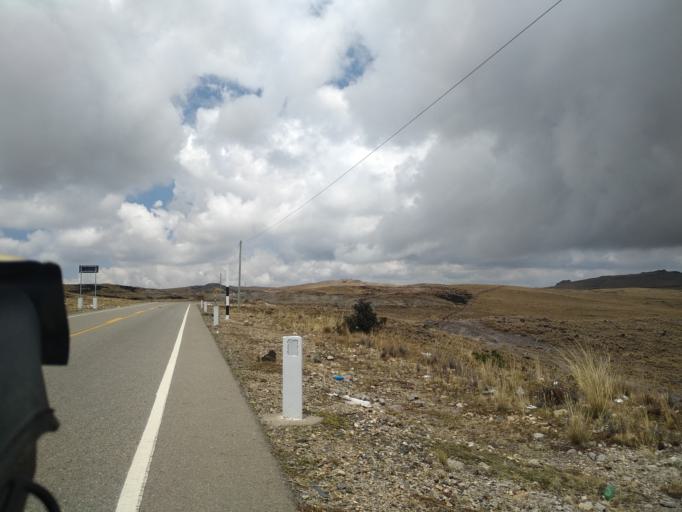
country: PE
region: La Libertad
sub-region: Provincia de Santiago de Chuco
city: Quiruvilca
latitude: -7.9386
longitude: -78.1849
